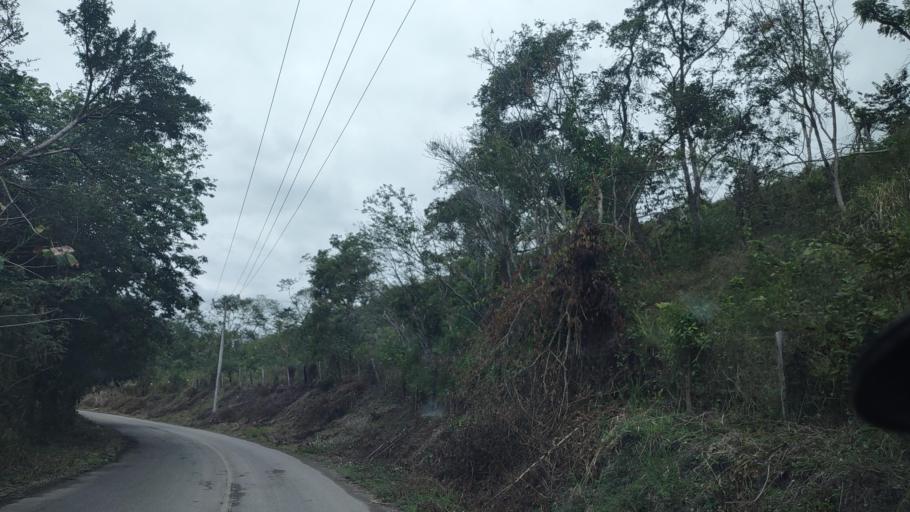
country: MX
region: Veracruz
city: Papantla de Olarte
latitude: 20.4438
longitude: -97.2884
